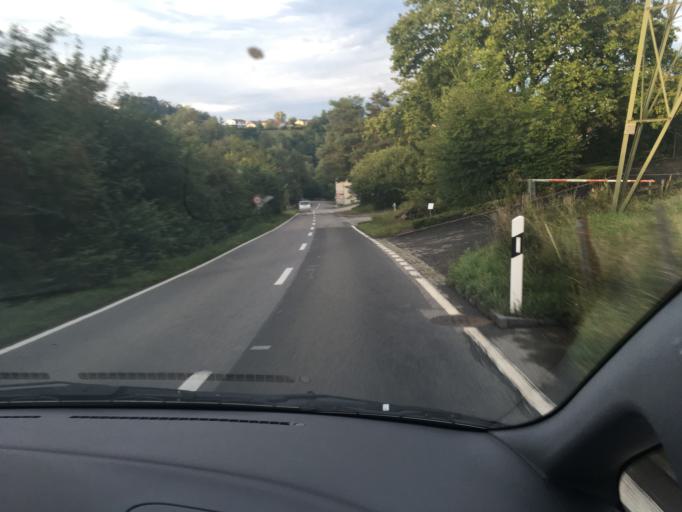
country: CH
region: Bern
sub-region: Bern-Mittelland District
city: Kirchlindach
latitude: 46.9720
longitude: 7.4261
